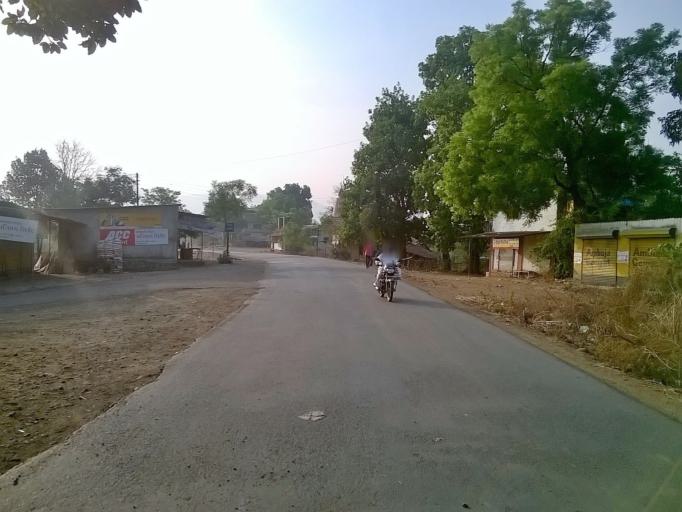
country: IN
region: Maharashtra
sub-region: Raigarh
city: Kalundri
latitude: 19.0182
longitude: 73.1906
